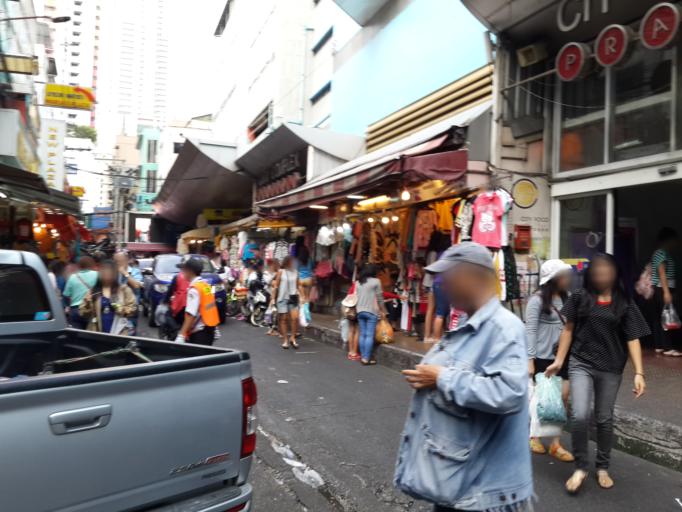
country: TH
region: Bangkok
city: Ratchathewi
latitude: 13.7511
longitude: 100.5394
